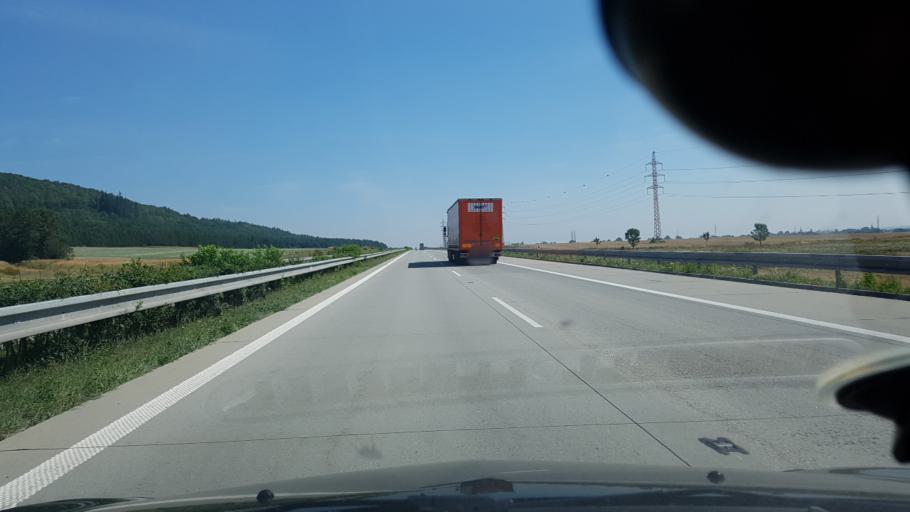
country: CZ
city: Jesenik nad Odrou
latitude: 49.6504
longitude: 17.8862
